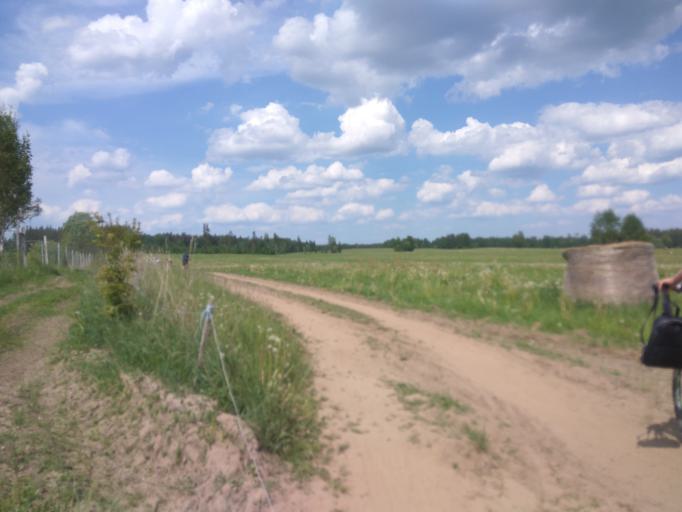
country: LV
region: Kuldigas Rajons
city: Kuldiga
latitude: 56.8930
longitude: 21.9262
